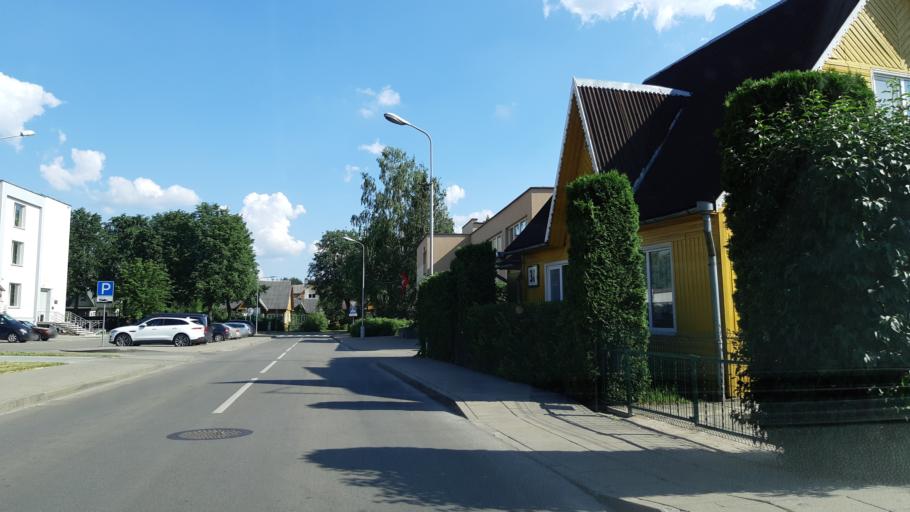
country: LT
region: Alytaus apskritis
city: Druskininkai
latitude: 54.0117
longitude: 23.9835
